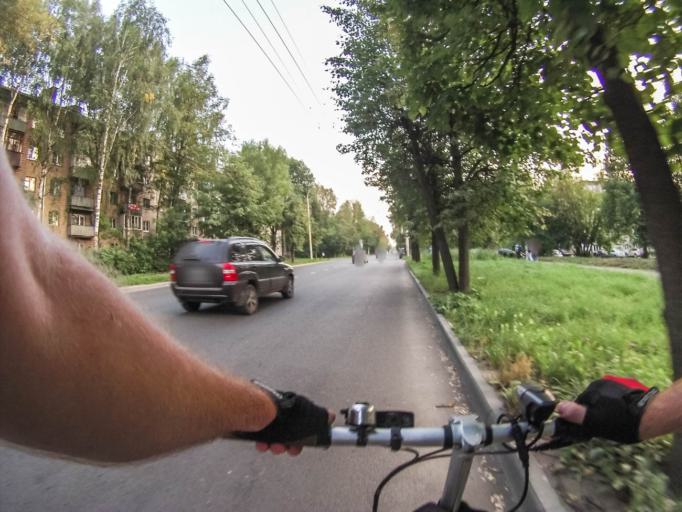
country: RU
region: Kostroma
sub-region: Kostromskoy Rayon
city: Kostroma
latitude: 57.7881
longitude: 40.9431
